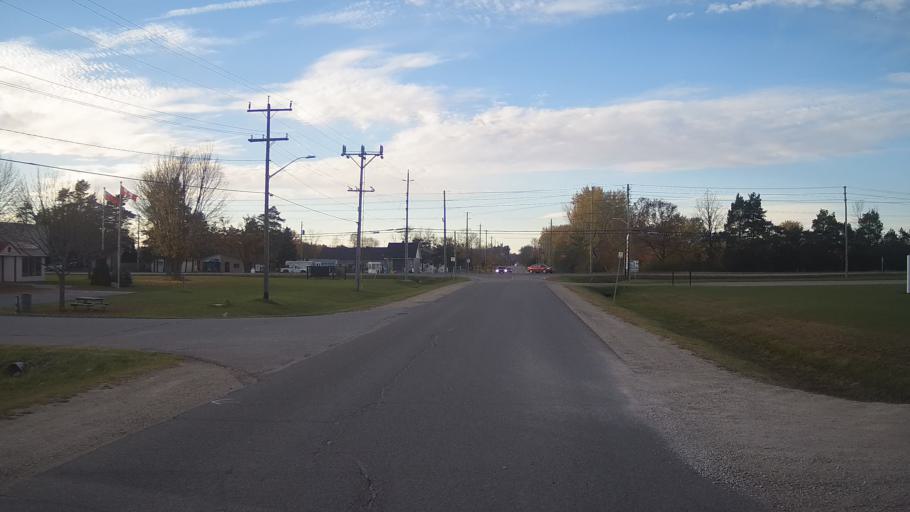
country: CA
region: Ontario
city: Perth
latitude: 44.8879
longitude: -76.2444
